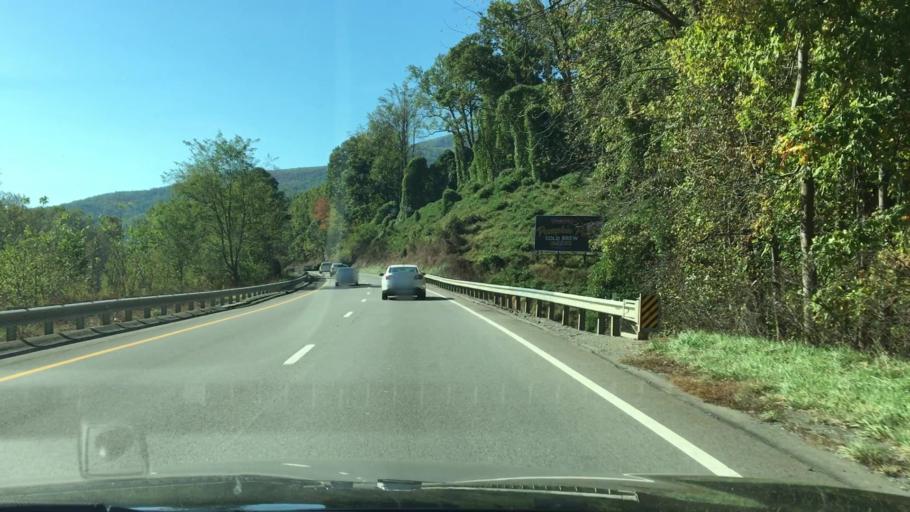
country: US
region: Virginia
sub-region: Roanoke County
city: Narrows
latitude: 37.1416
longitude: -79.9720
